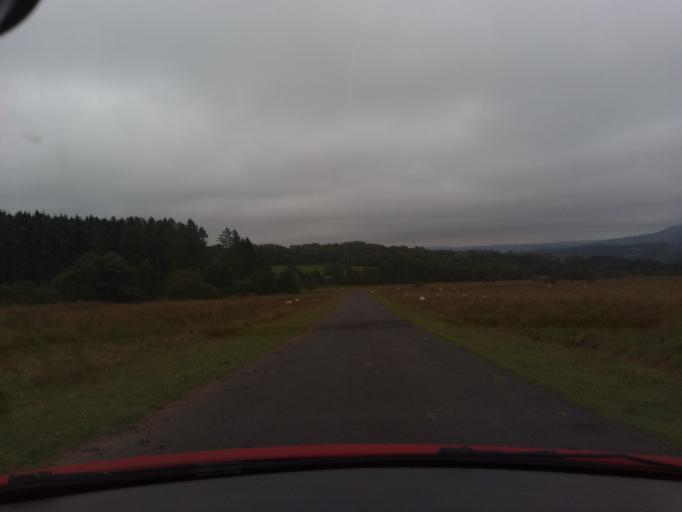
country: GB
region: England
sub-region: Northumberland
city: Otterburn
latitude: 55.2708
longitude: -2.1080
